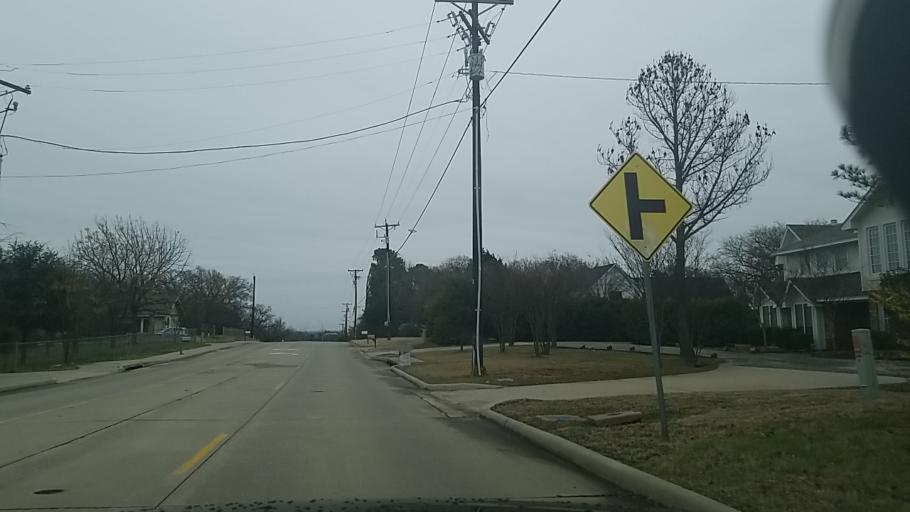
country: US
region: Texas
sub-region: Denton County
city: Corinth
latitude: 33.1541
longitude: -97.0671
